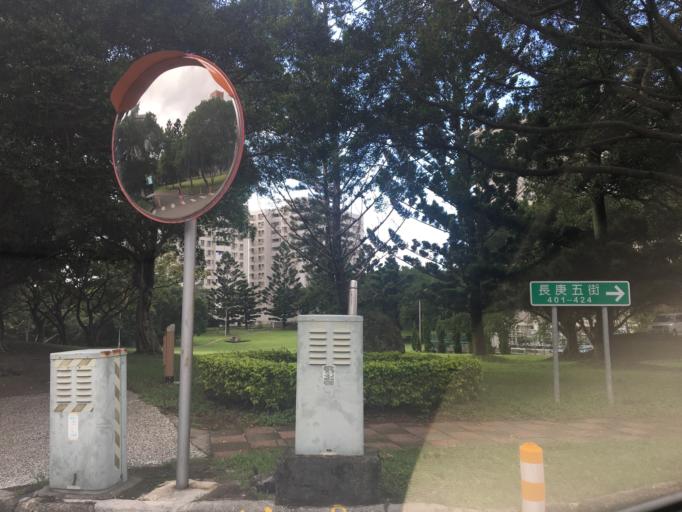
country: TW
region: Taipei
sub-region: Taipei
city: Banqiao
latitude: 25.0612
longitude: 121.3864
